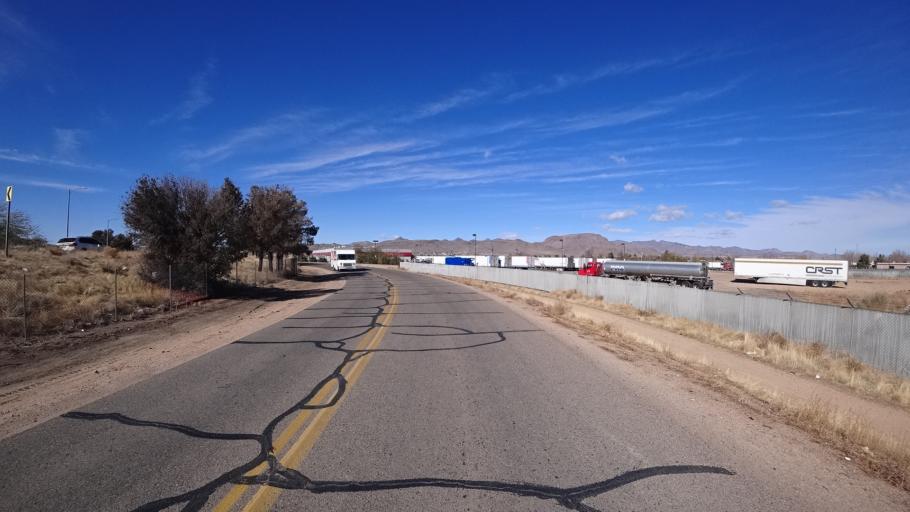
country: US
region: Arizona
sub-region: Mohave County
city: New Kingman-Butler
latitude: 35.2194
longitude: -114.0121
